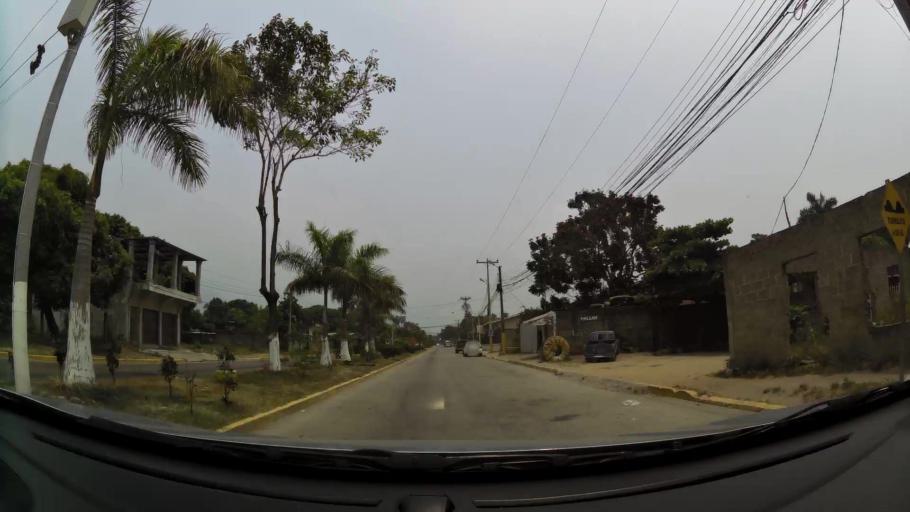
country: HN
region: Yoro
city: El Progreso
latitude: 15.4016
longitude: -87.8139
